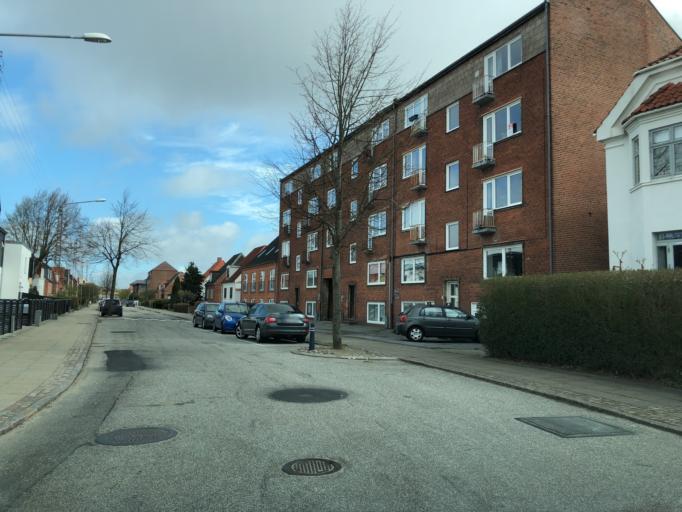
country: DK
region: North Denmark
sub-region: Alborg Kommune
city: Aalborg
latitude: 57.0510
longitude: 9.8958
